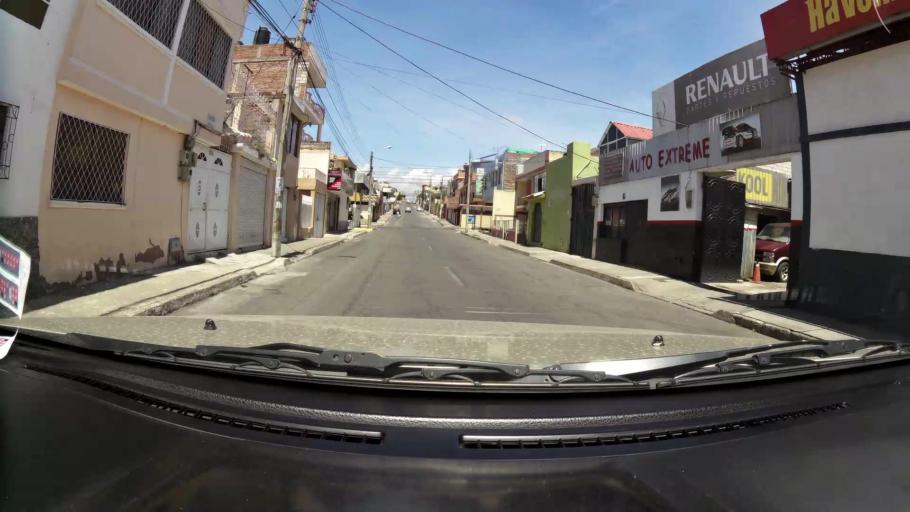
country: EC
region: Chimborazo
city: Riobamba
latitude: -1.6642
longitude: -78.6544
